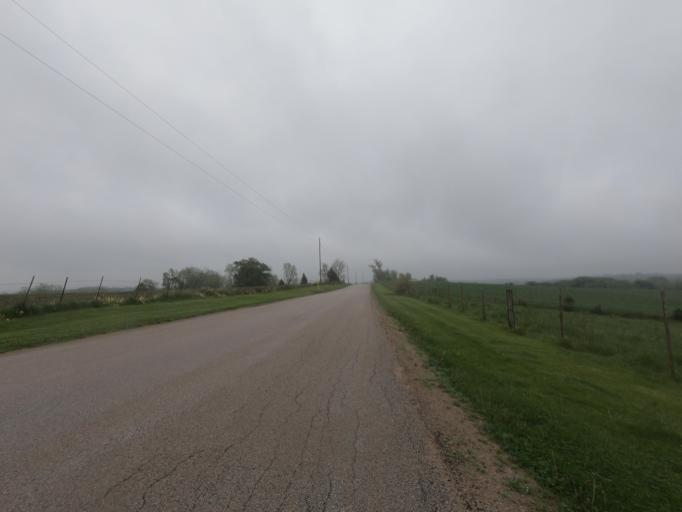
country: US
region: Wisconsin
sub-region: Grant County
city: Hazel Green
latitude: 42.4961
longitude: -90.4999
